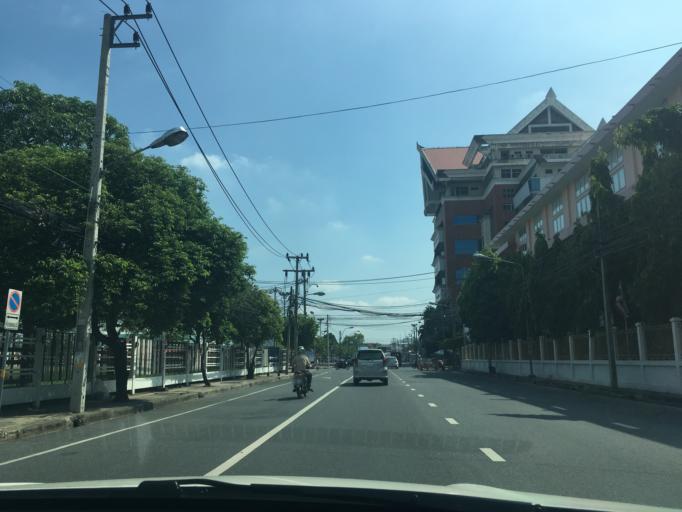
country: TH
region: Chon Buri
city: Chon Buri
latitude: 13.3619
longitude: 100.9804
